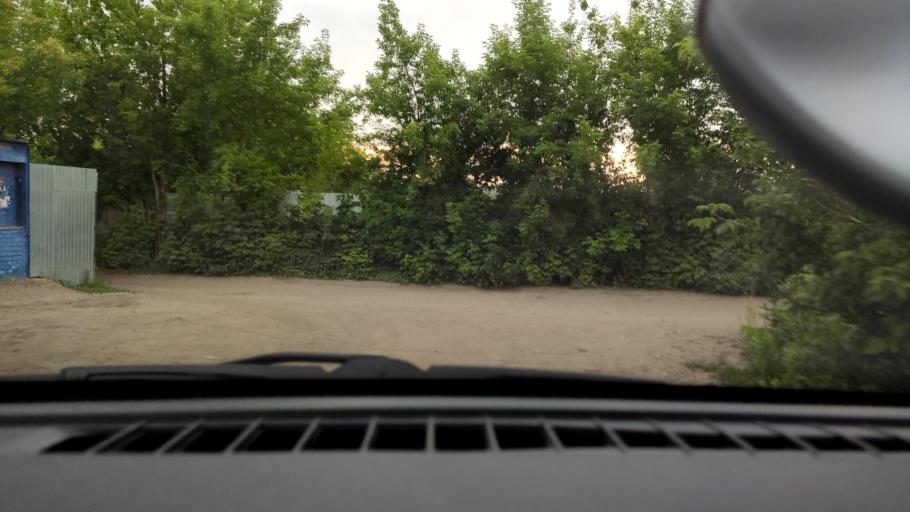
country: RU
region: Samara
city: Petra-Dubrava
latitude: 53.2782
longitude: 50.3247
